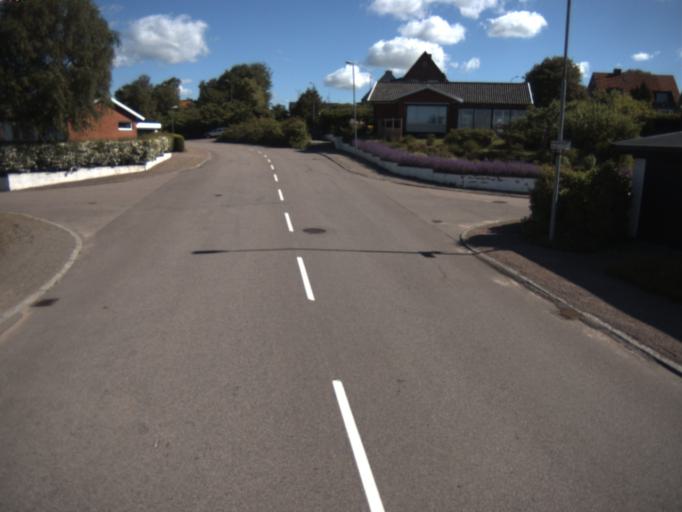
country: SE
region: Skane
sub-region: Helsingborg
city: Rydeback
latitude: 55.9961
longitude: 12.7487
